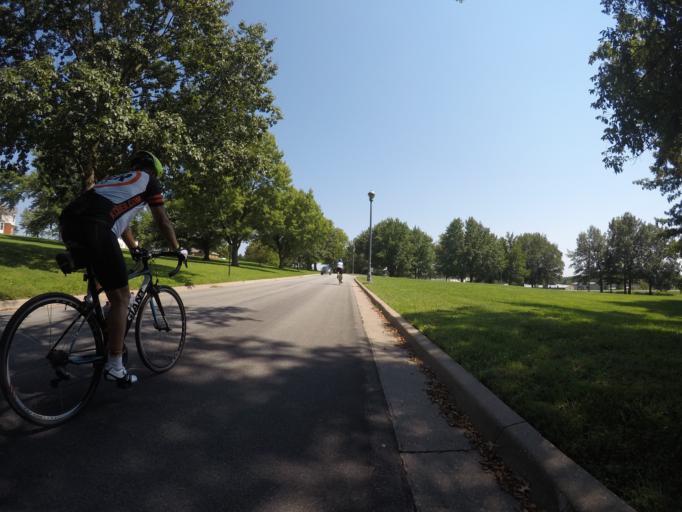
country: US
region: Kansas
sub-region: Leavenworth County
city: Lansing
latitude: 39.2755
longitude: -94.8958
